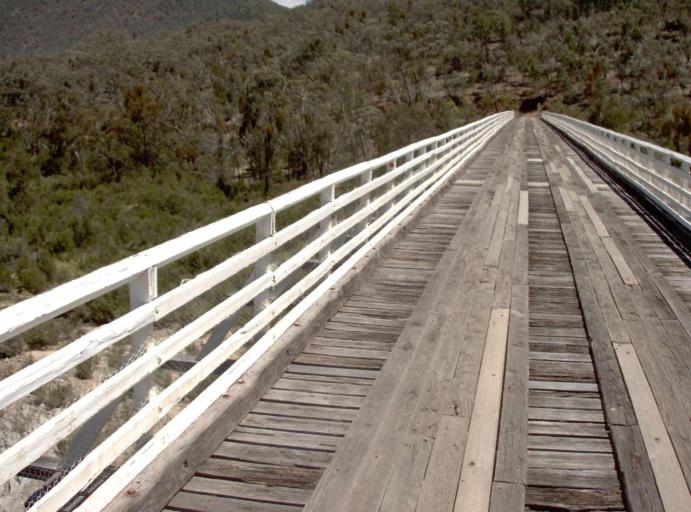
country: AU
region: New South Wales
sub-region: Snowy River
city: Jindabyne
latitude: -37.0840
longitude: 148.4135
